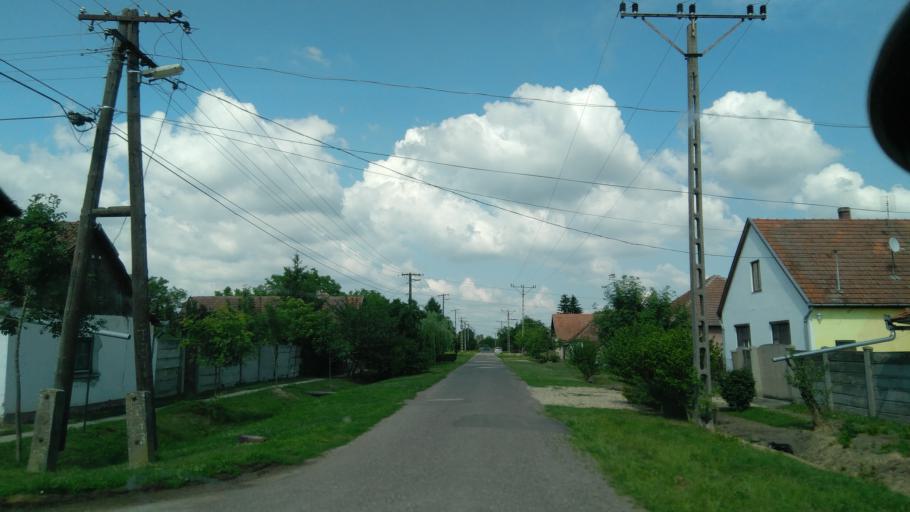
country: HU
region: Bekes
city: Doboz
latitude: 46.7286
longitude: 21.2440
